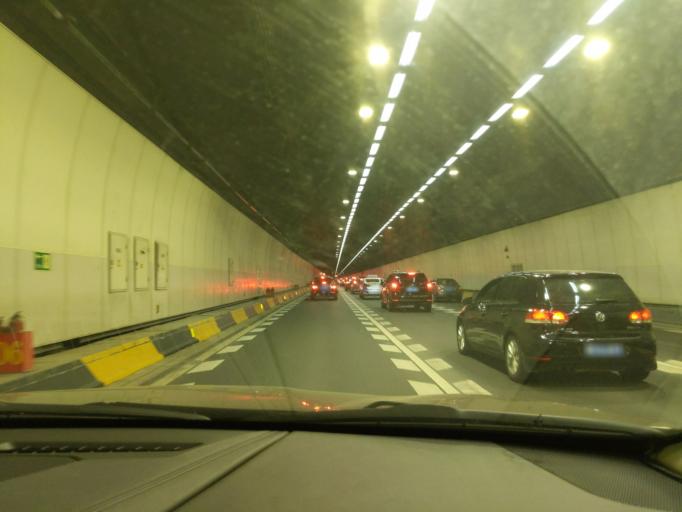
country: CN
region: Fujian
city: Liuwudian
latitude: 24.5180
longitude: 118.1813
